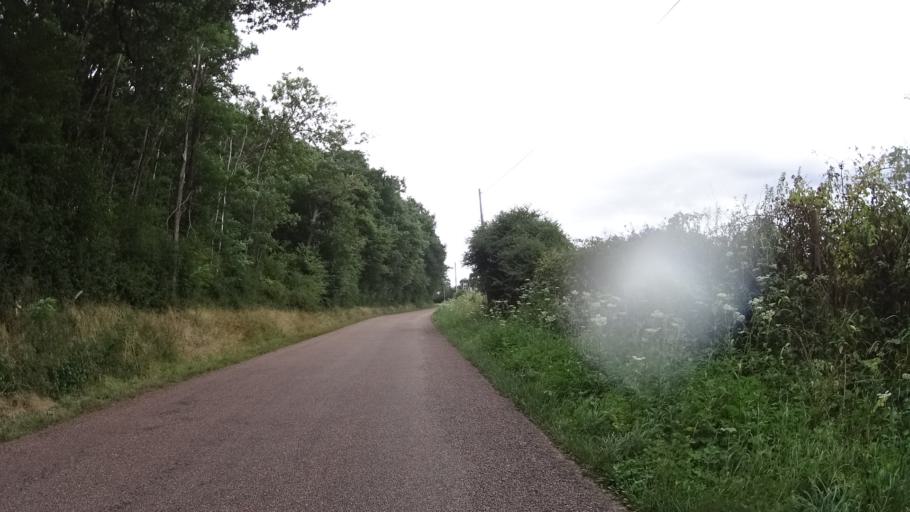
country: FR
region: Centre
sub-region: Departement du Loiret
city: Saint-Germain-des-Pres
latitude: 47.9417
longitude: 2.8603
